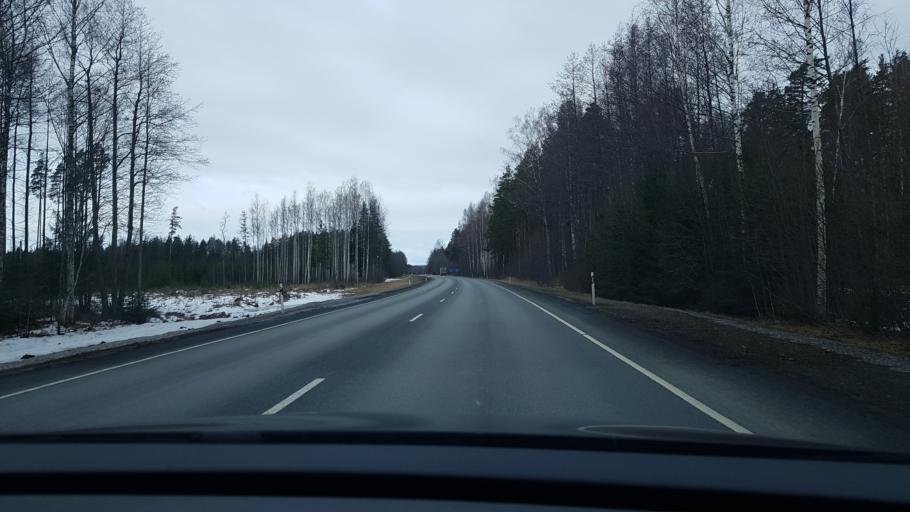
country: EE
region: Paernumaa
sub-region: Paikuse vald
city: Paikuse
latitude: 58.2557
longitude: 24.6795
